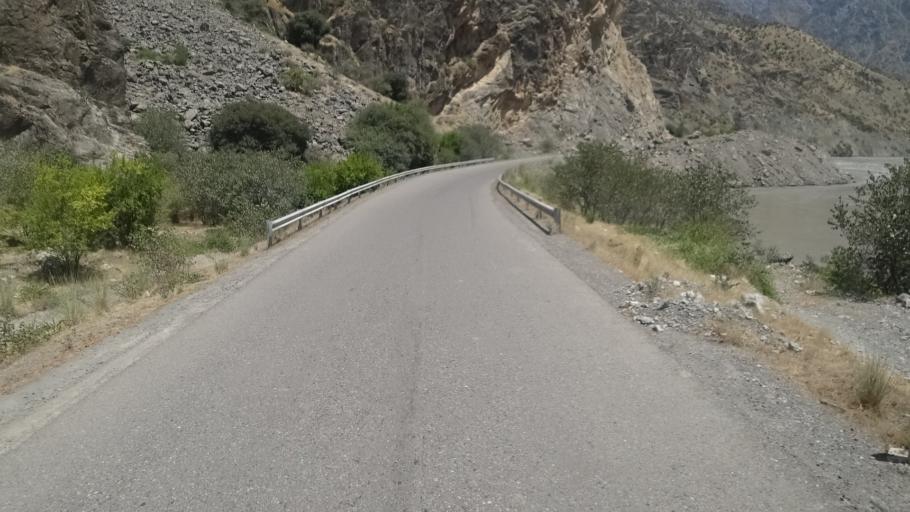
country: AF
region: Badakhshan
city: Deh Khwahan
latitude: 37.9457
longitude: 70.2477
